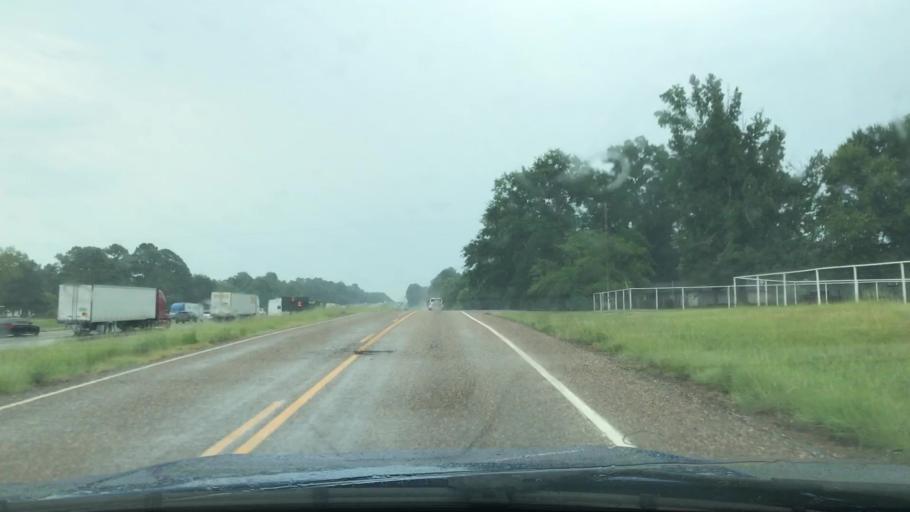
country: US
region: Texas
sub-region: Harrison County
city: Waskom
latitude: 32.4865
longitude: -94.1294
